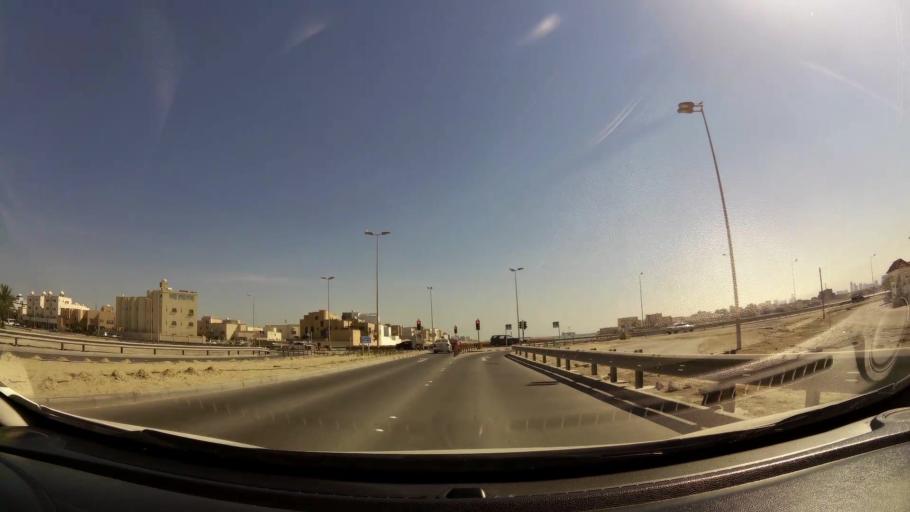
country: BH
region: Muharraq
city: Al Hadd
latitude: 26.2476
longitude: 50.6404
